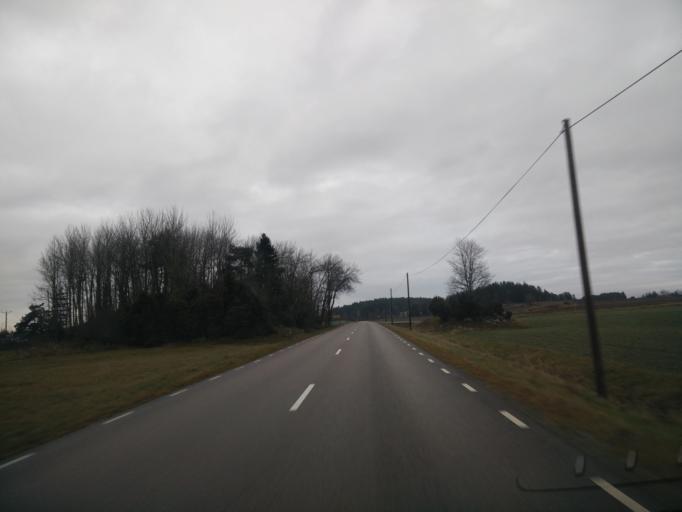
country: SE
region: Uppsala
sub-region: Enkopings Kommun
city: Enkoping
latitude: 59.8026
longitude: 17.0968
